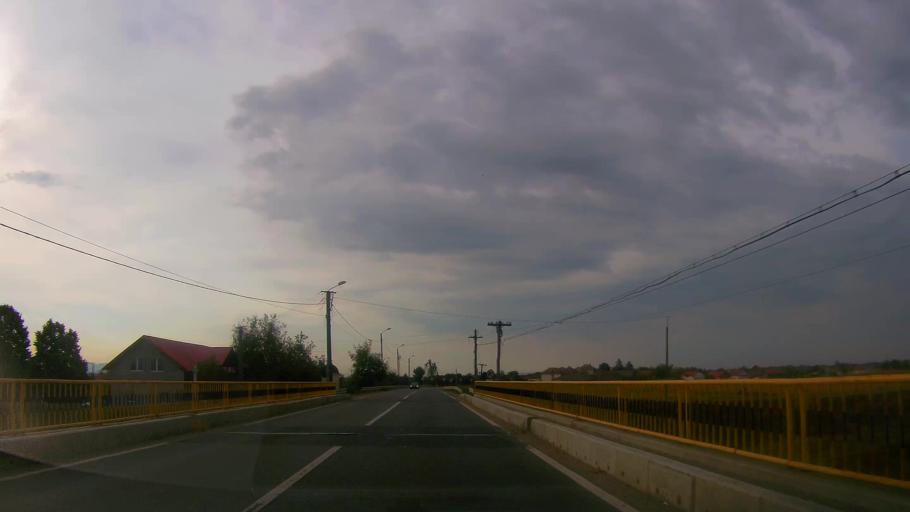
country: RO
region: Satu Mare
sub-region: Comuna Turulung
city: Turulung
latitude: 47.9289
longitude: 23.0852
